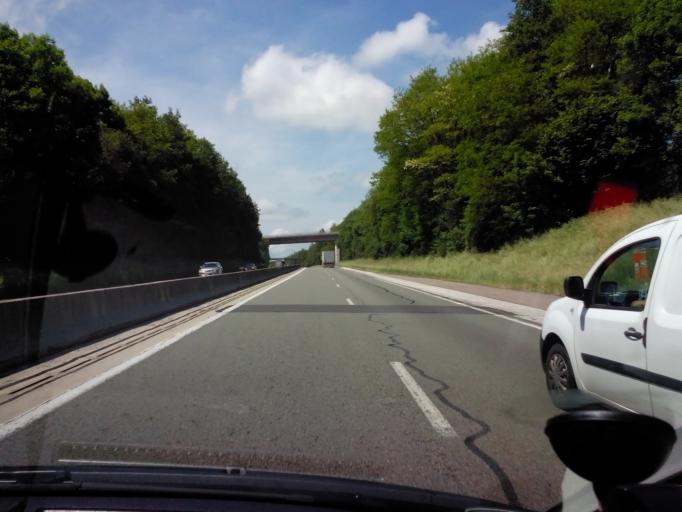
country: FR
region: Champagne-Ardenne
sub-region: Departement de la Haute-Marne
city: Avrecourt
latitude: 47.9658
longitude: 5.4797
